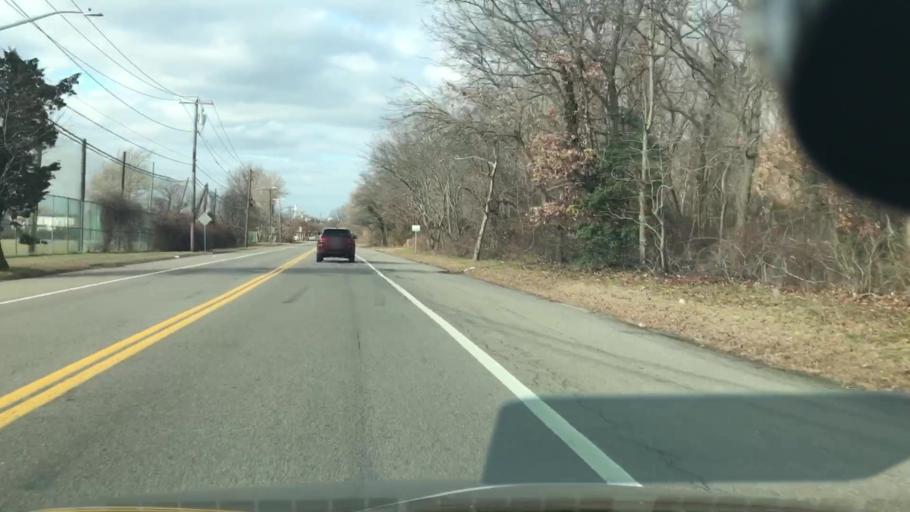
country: US
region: New York
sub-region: Suffolk County
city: Babylon
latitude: 40.6830
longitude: -73.3422
